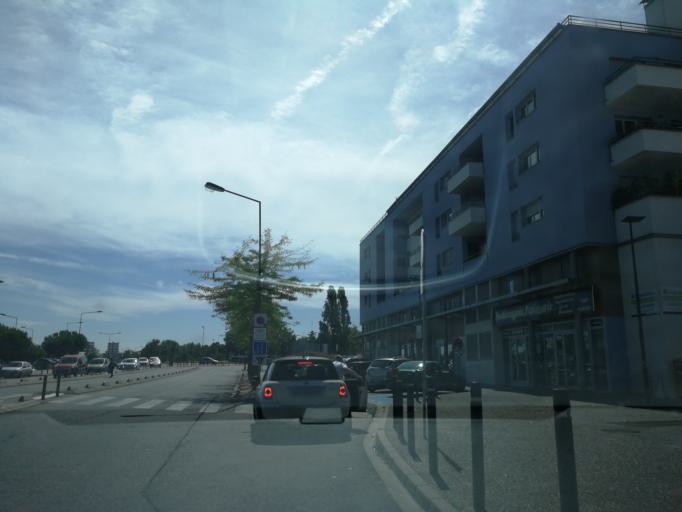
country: FR
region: Midi-Pyrenees
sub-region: Departement de la Haute-Garonne
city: Ramonville-Saint-Agne
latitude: 43.5558
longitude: 1.4763
